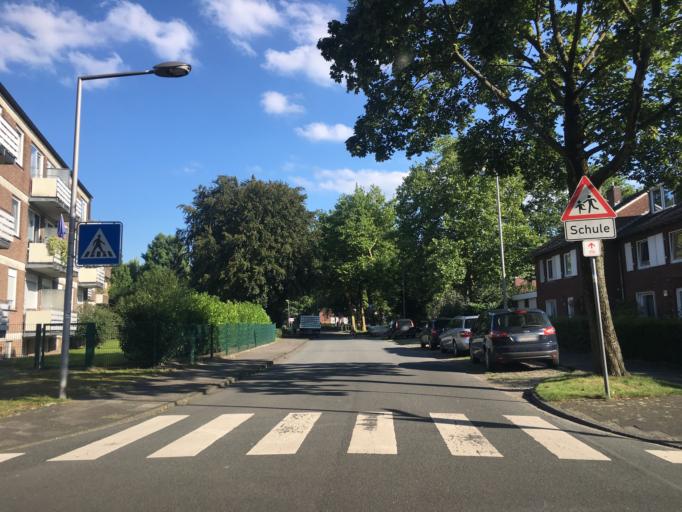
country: DE
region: North Rhine-Westphalia
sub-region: Regierungsbezirk Munster
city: Muenster
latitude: 51.9427
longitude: 7.6044
